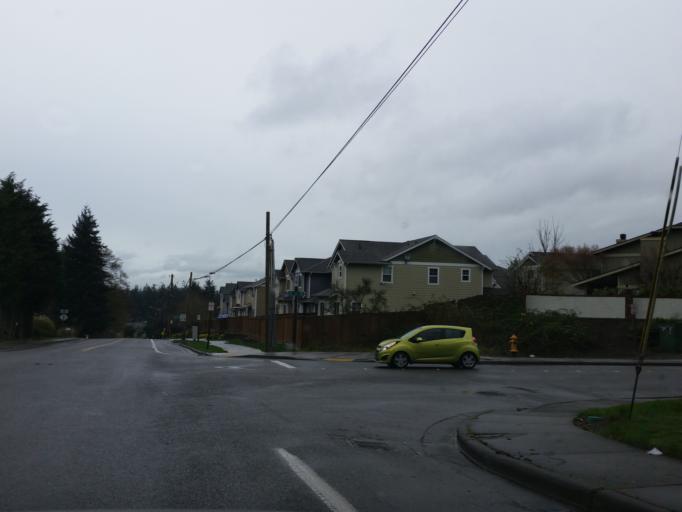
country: US
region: Washington
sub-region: Snohomish County
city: Martha Lake
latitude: 47.8781
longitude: -122.2493
